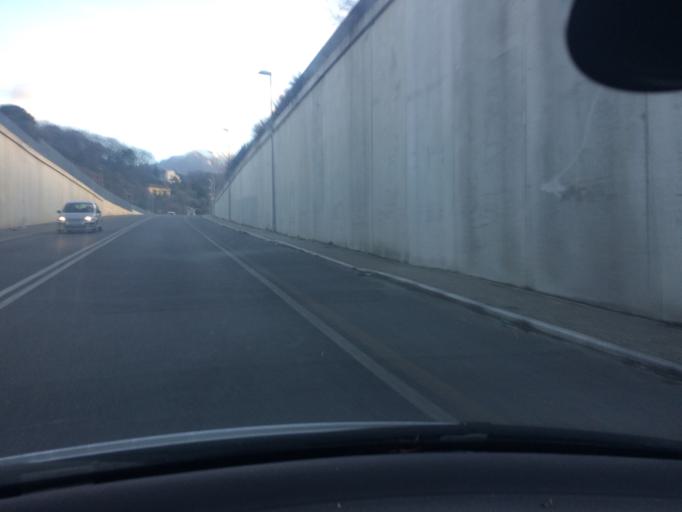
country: IT
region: Tuscany
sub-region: Provincia di Massa-Carrara
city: Massa
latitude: 44.0348
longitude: 10.0996
